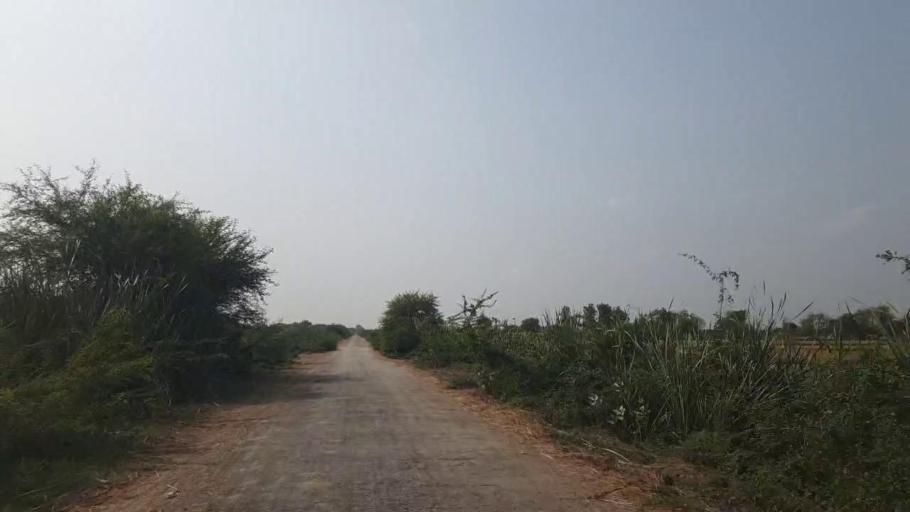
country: PK
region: Sindh
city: Talhar
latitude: 24.7669
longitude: 68.7653
